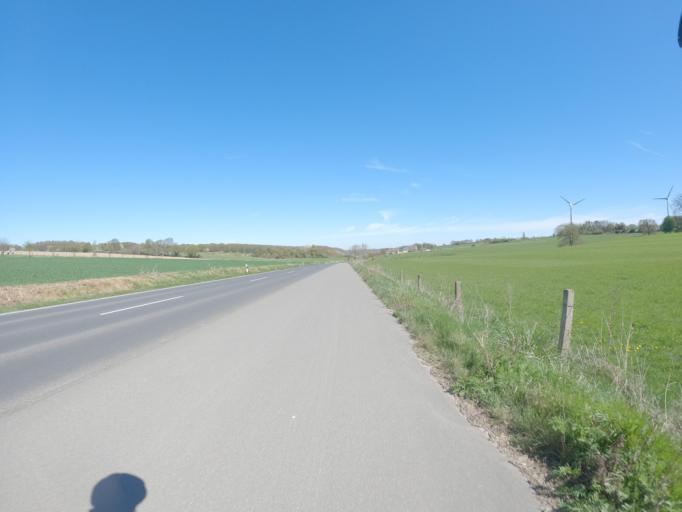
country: DE
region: North Rhine-Westphalia
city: Stolberg
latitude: 50.7787
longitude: 6.2614
